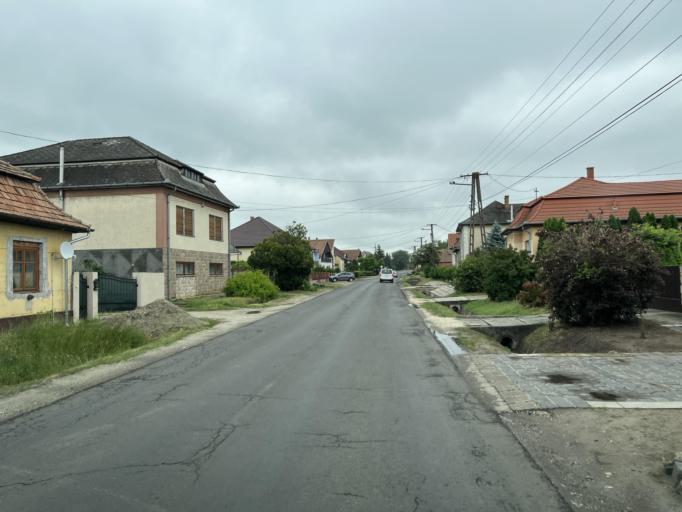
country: HU
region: Pest
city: Galgaheviz
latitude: 47.6190
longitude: 19.5676
